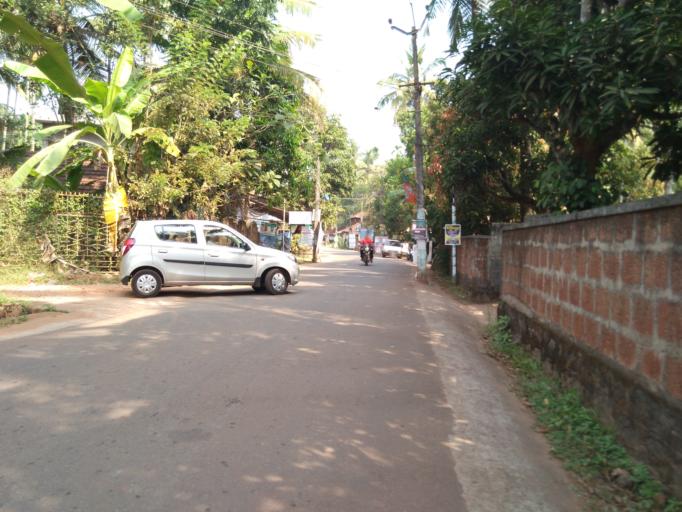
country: IN
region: Kerala
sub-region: Kozhikode
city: Kunnamangalam
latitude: 11.2907
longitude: 75.8362
